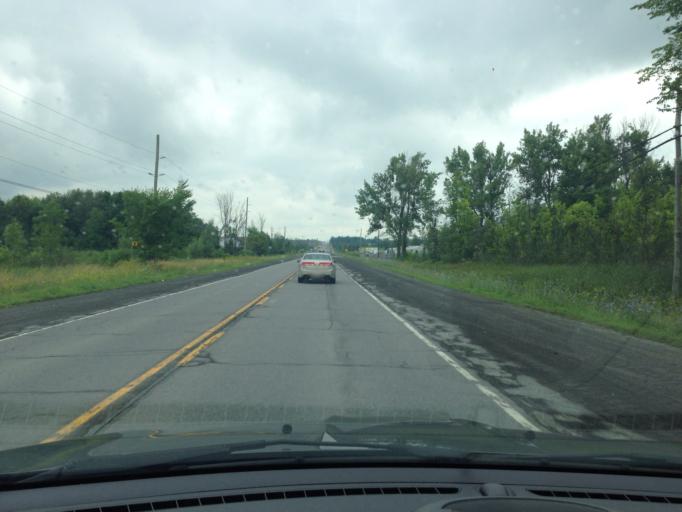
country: CA
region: Ontario
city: Ottawa
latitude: 45.3100
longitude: -75.5876
